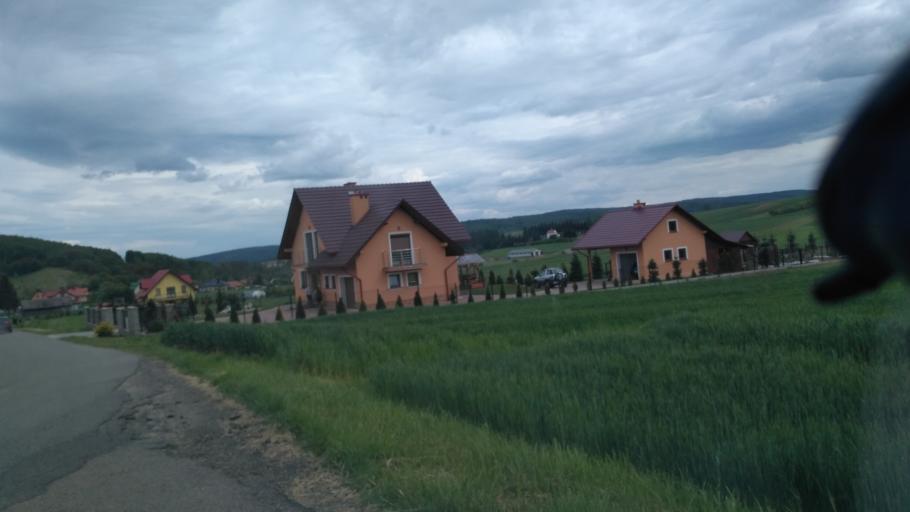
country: PL
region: Subcarpathian Voivodeship
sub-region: Powiat przemyski
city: Przedmiescie Dubieckie
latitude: 49.8349
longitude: 22.3170
